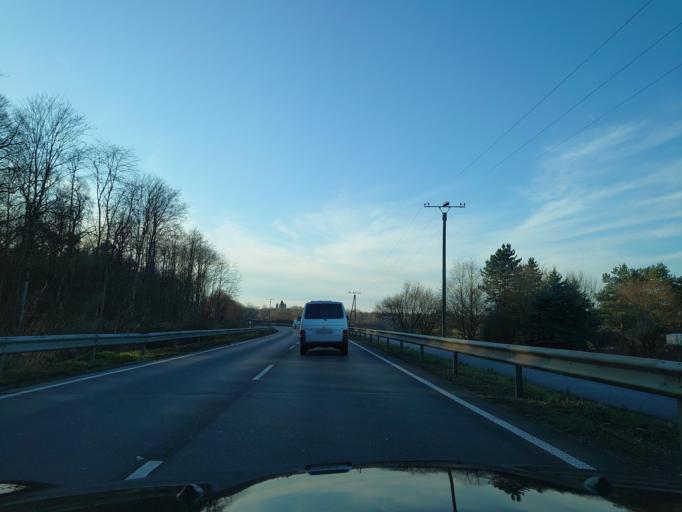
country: DE
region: North Rhine-Westphalia
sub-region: Regierungsbezirk Dusseldorf
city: Dormagen
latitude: 51.0776
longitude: 6.7656
